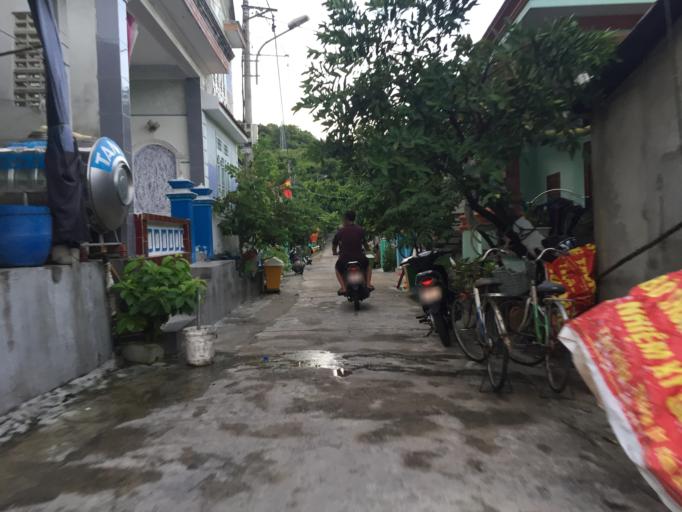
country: VN
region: Quang Nam
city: Hoi An
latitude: 15.9551
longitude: 108.5080
